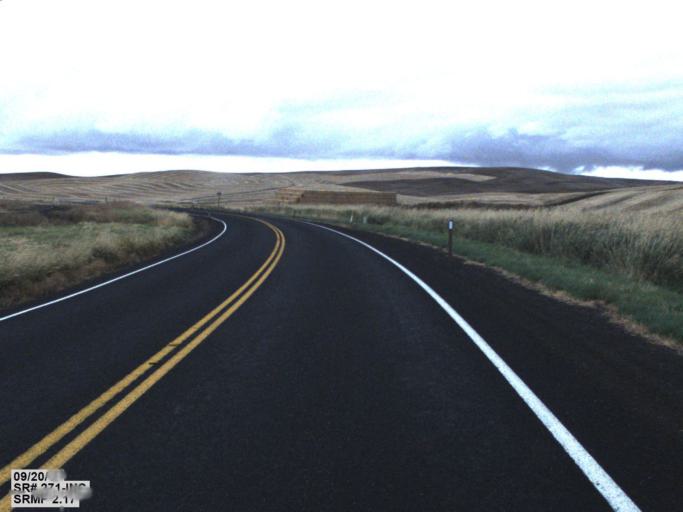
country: US
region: Washington
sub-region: Whitman County
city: Colfax
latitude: 47.1609
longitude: -117.2670
